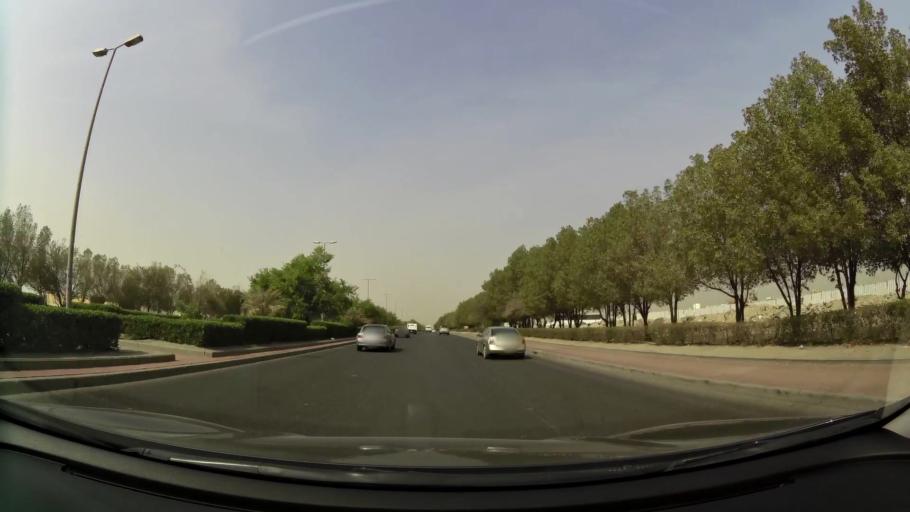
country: KW
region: Al Asimah
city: Ar Rabiyah
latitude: 29.2554
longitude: 47.9195
